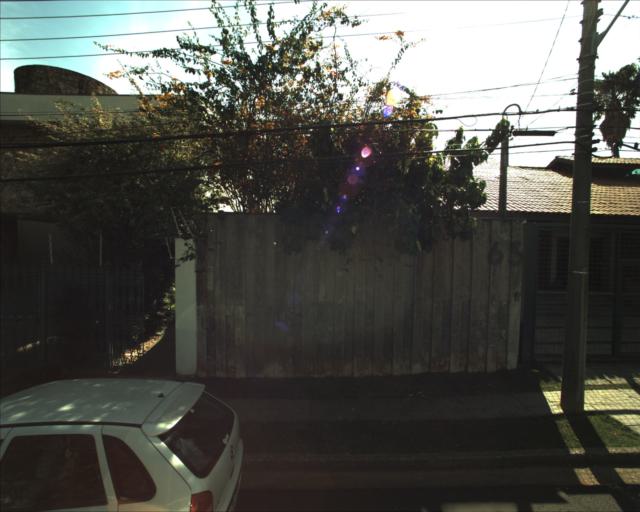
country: BR
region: Sao Paulo
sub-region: Sorocaba
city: Sorocaba
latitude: -23.4900
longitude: -47.4465
